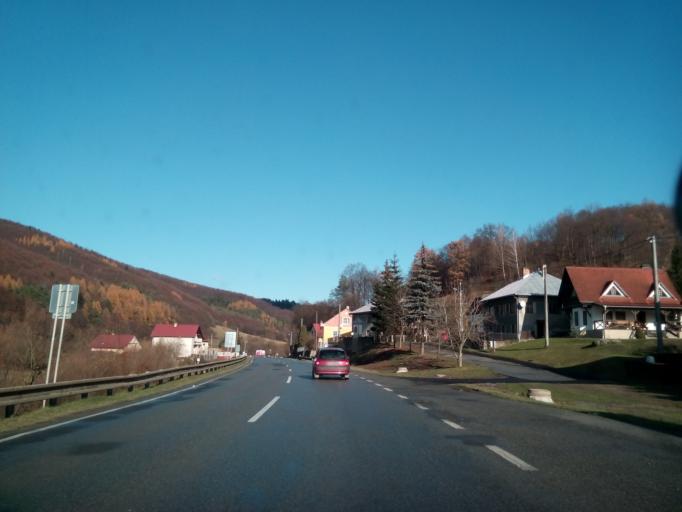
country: SK
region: Presovsky
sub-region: Okres Bardejov
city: Bardejov
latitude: 49.2583
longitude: 21.2508
